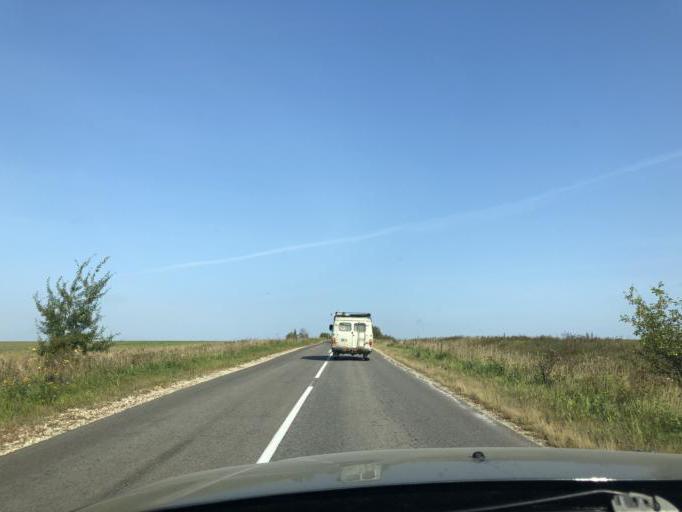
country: RU
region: Tula
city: Novogurovskiy
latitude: 54.4017
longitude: 37.3127
